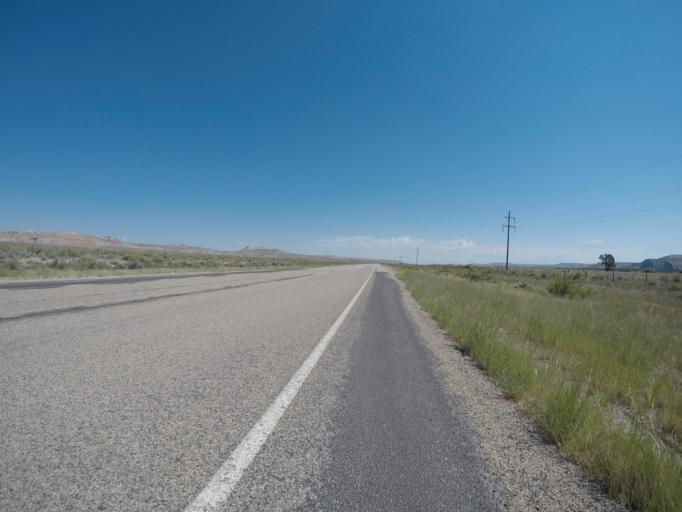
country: US
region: Wyoming
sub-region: Sublette County
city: Marbleton
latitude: 42.3462
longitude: -110.1622
